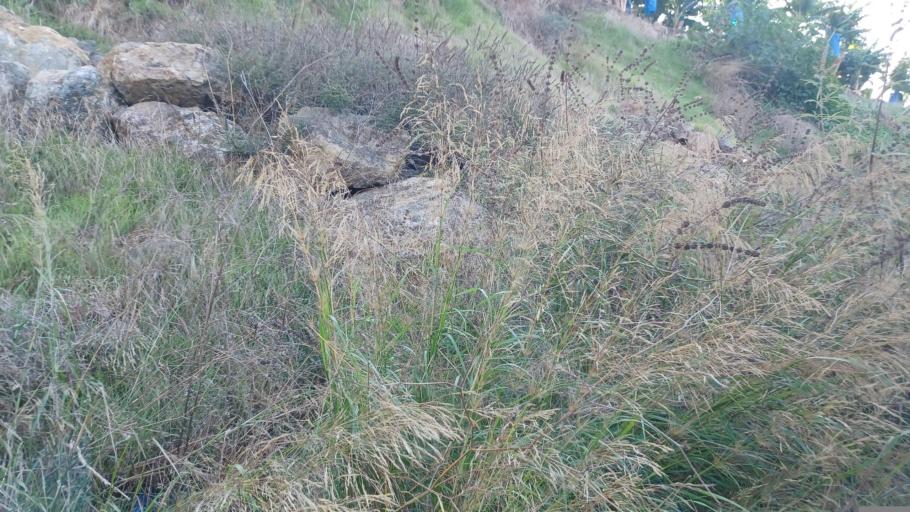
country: CY
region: Pafos
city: Kissonerga
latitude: 34.8354
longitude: 32.3949
